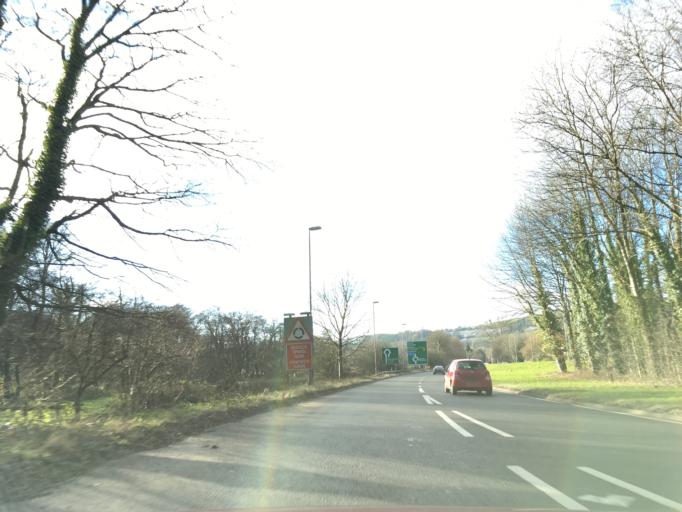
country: GB
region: Wales
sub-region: Torfaen County Borough
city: New Inn
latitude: 51.7178
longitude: -2.9913
